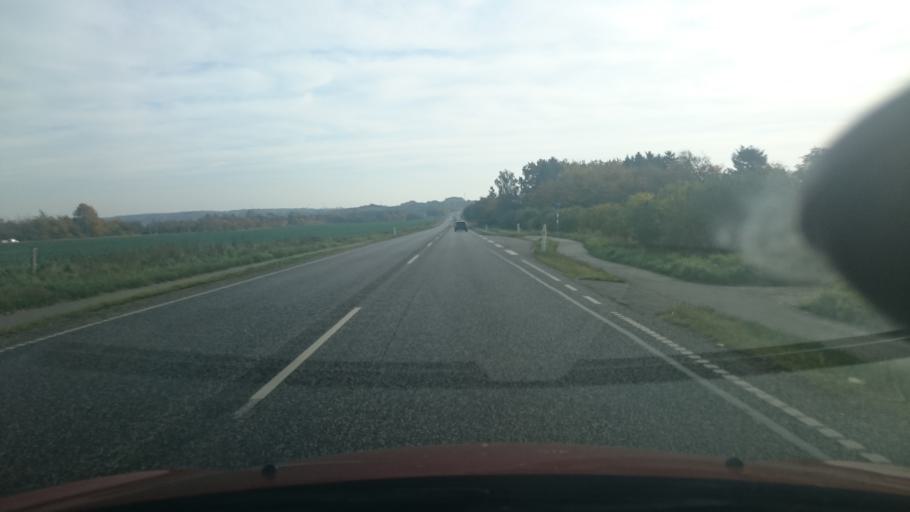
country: DK
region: Central Jutland
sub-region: Randers Kommune
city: Assentoft
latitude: 56.4416
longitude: 10.1009
